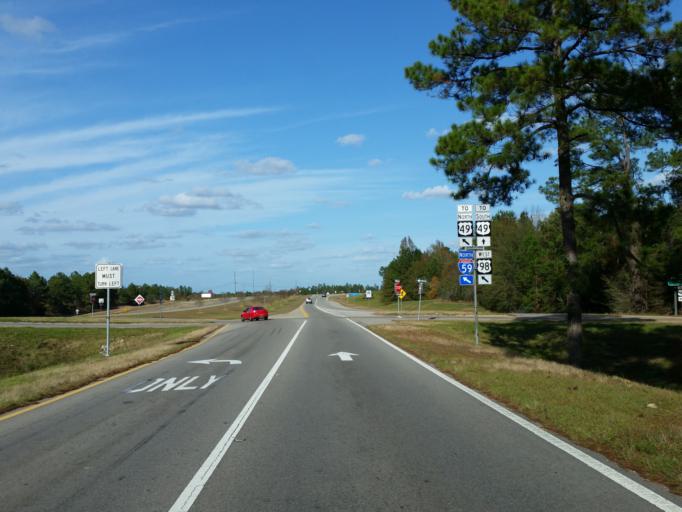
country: US
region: Mississippi
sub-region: Lamar County
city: West Hattiesburg
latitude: 31.2607
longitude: -89.3371
